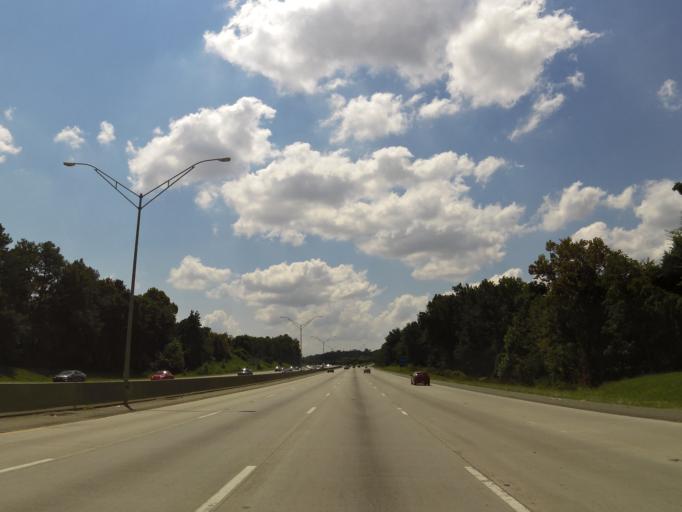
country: US
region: North Carolina
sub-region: Cabarrus County
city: Harrisburg
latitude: 35.3187
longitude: -80.7533
